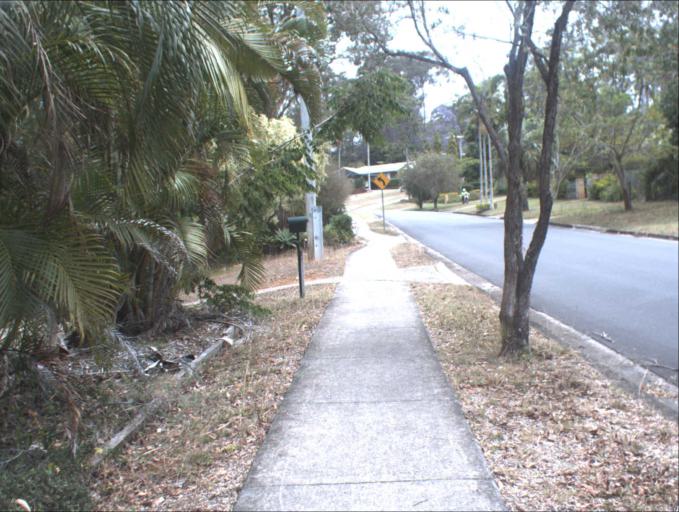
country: AU
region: Queensland
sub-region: Logan
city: Slacks Creek
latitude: -27.6713
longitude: 153.1750
